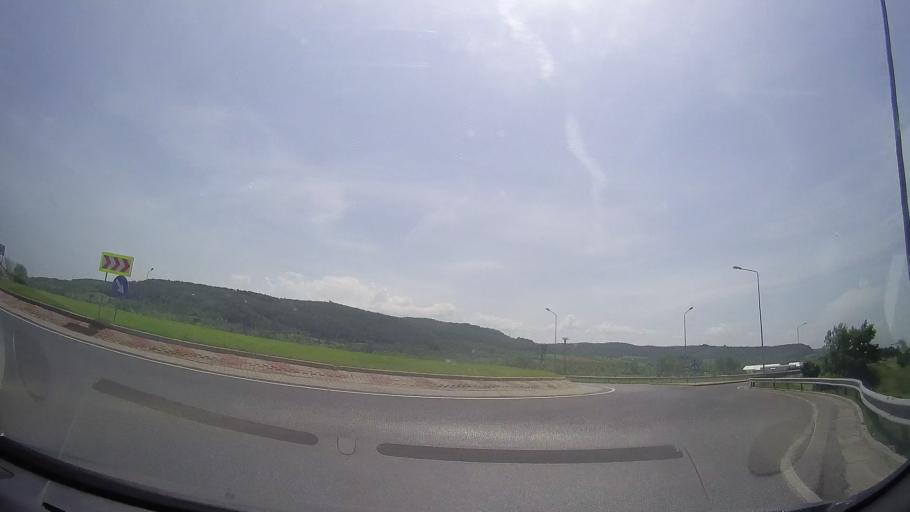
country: RO
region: Hunedoara
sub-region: Oras Simeria
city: Simeria
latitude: 45.8343
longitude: 23.0388
